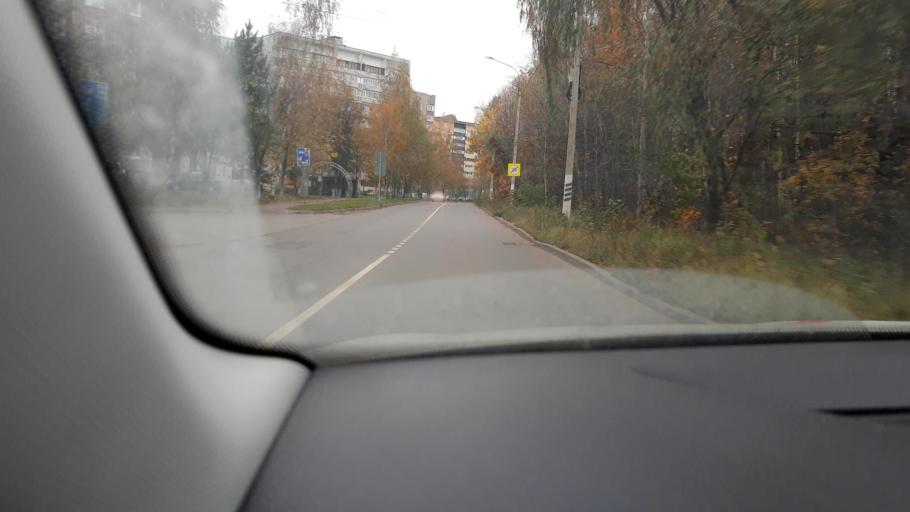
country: RU
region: Moskovskaya
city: Shcherbinka
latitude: 55.5337
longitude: 37.5879
